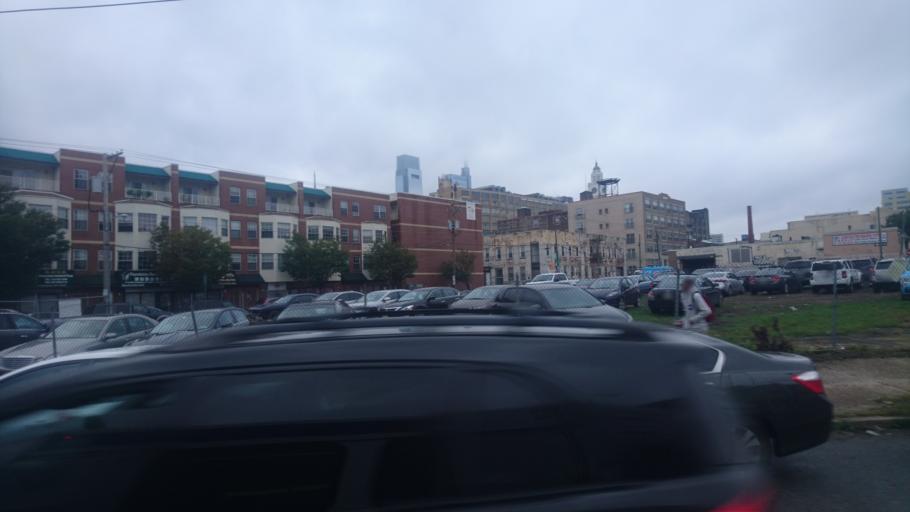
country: US
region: Pennsylvania
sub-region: Philadelphia County
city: Philadelphia
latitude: 39.9612
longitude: -75.1571
